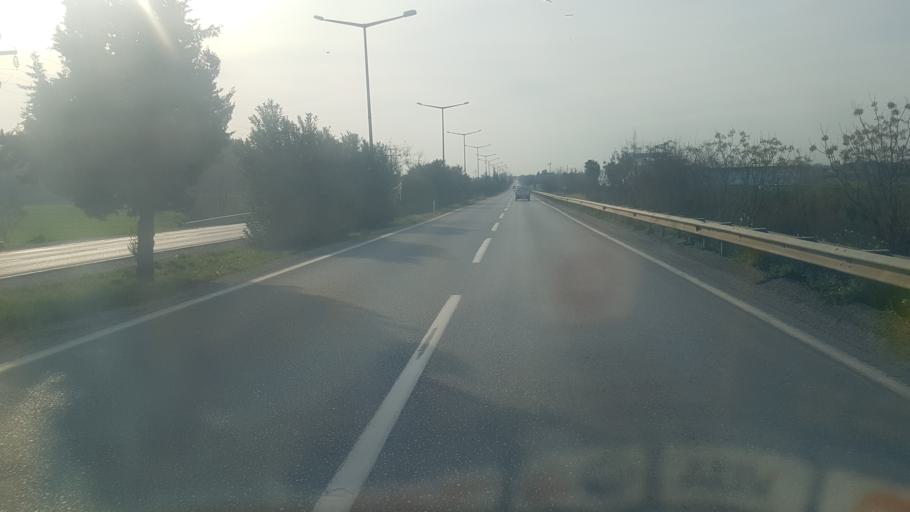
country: TR
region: Osmaniye
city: Toprakkale
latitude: 37.0532
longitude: 36.1459
